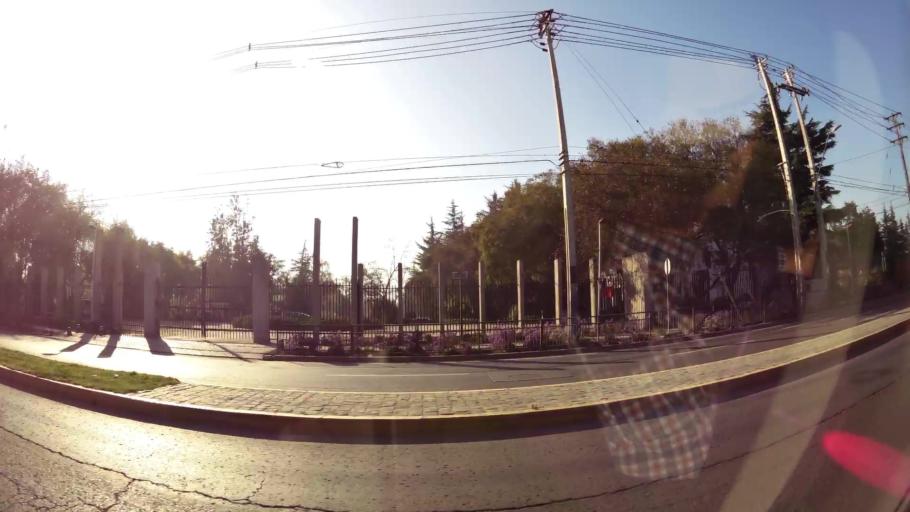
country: CL
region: Santiago Metropolitan
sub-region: Provincia de Santiago
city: Santiago
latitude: -33.3817
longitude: -70.6399
